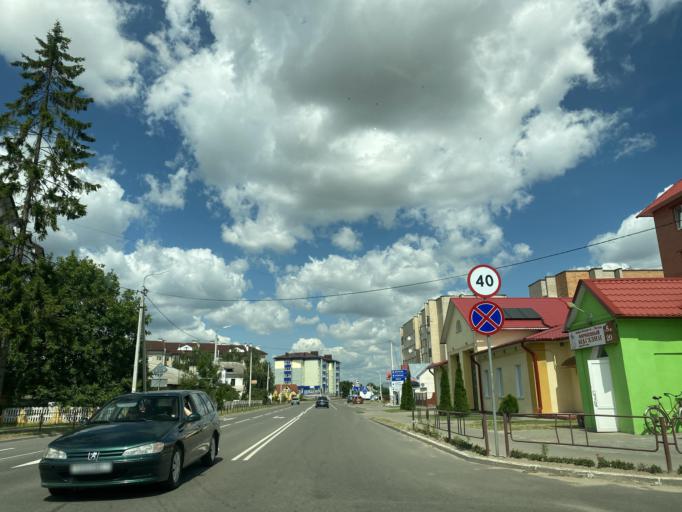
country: BY
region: Brest
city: Ivanava
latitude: 52.1473
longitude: 25.5420
